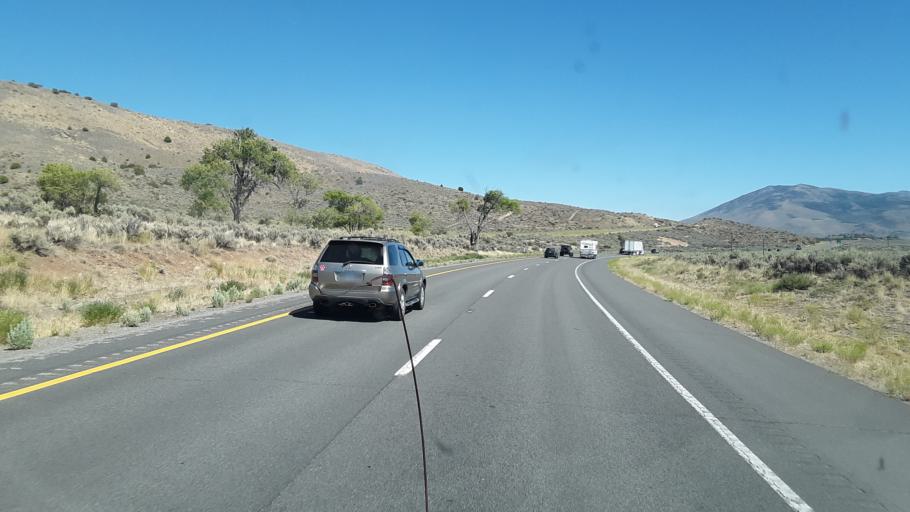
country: US
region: Nevada
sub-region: Washoe County
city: Cold Springs
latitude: 39.6909
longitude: -120.0168
